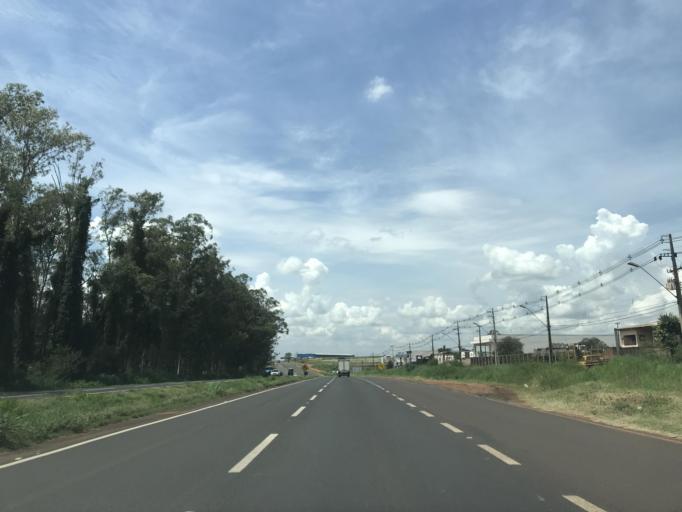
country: BR
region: Parana
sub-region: Alto Parana
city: Alto Parana
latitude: -23.2058
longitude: -52.1946
